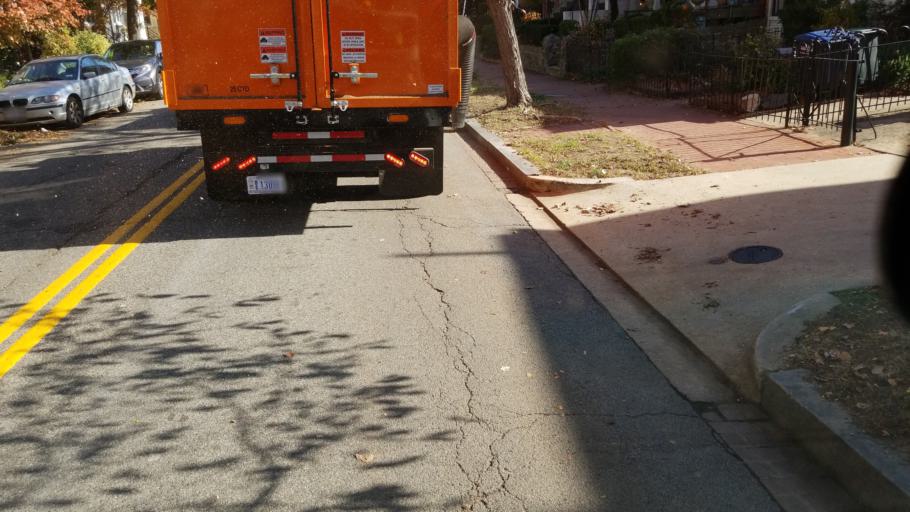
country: US
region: Washington, D.C.
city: Washington, D.C.
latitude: 38.8916
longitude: -76.9972
